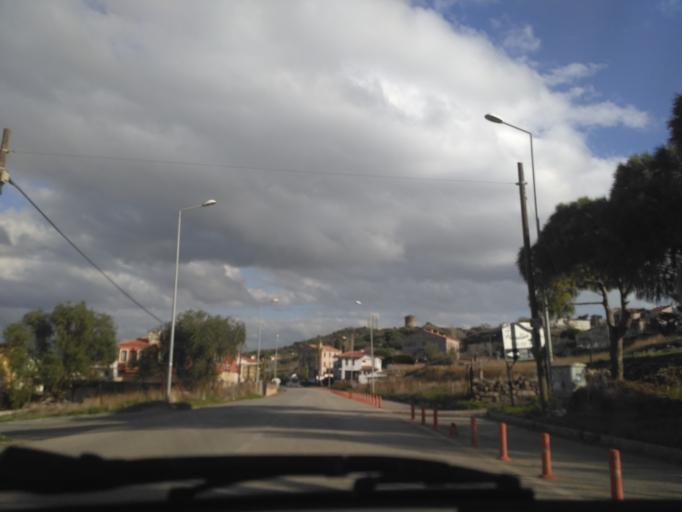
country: TR
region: Balikesir
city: Ayvalik
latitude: 39.3373
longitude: 26.6585
